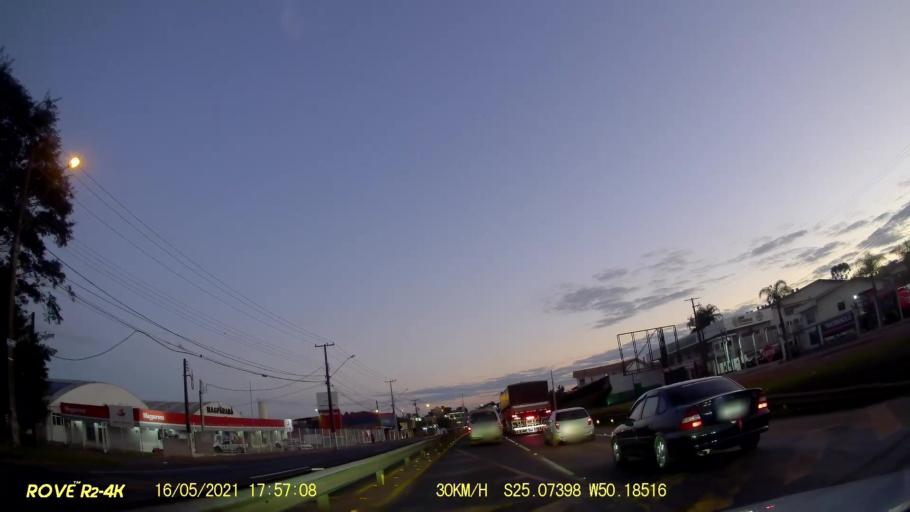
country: BR
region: Parana
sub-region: Ponta Grossa
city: Ponta Grossa
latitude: -25.0739
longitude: -50.1851
